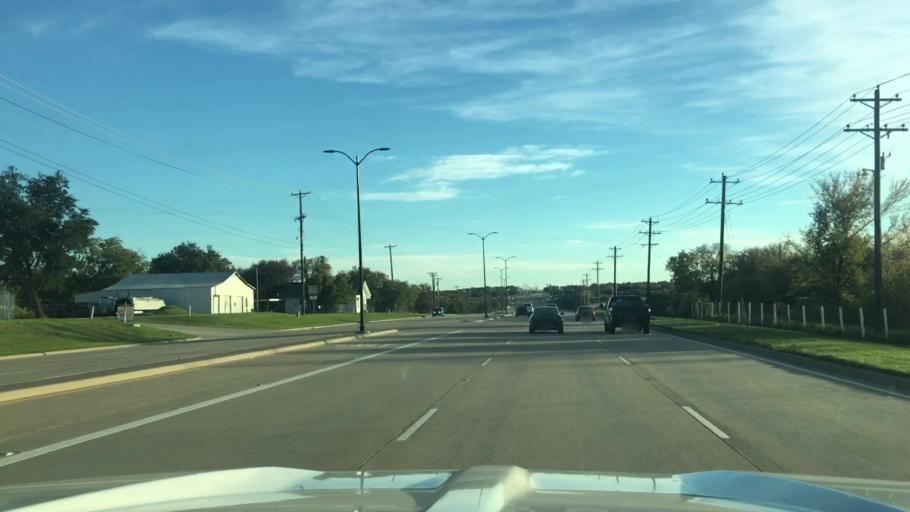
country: US
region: Texas
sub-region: Collin County
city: Frisco
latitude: 33.1832
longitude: -96.8031
